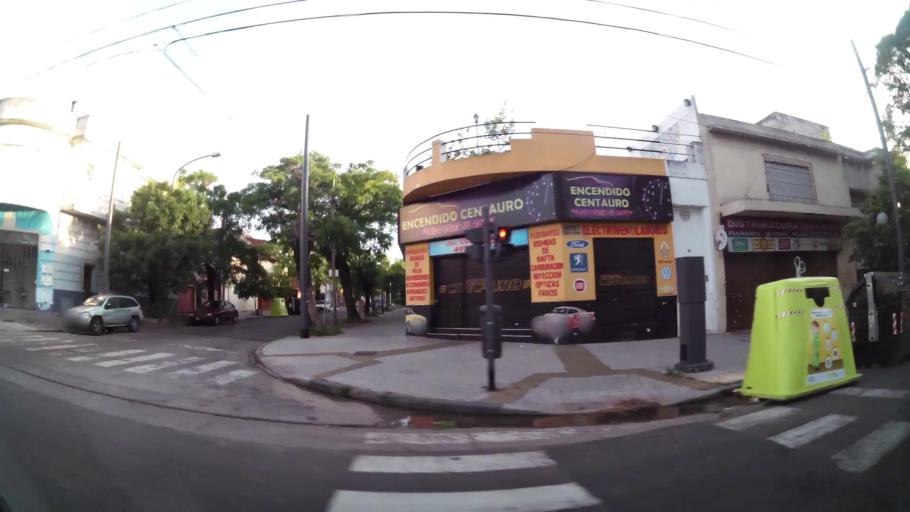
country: AR
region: Buenos Aires F.D.
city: Villa Lugano
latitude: -34.6414
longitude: -58.4301
